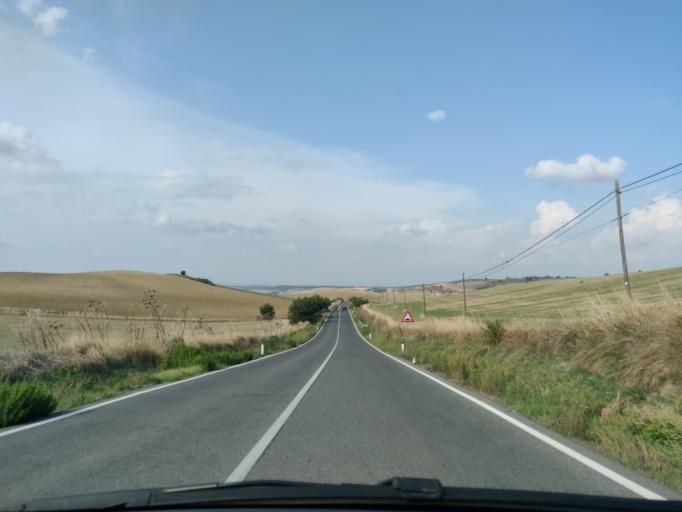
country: IT
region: Latium
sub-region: Provincia di Viterbo
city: Tarquinia
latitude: 42.2457
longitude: 11.8090
